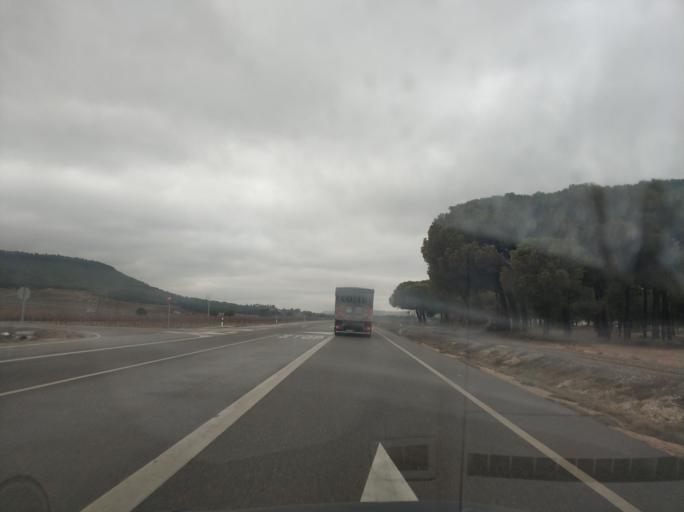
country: ES
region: Castille and Leon
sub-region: Provincia de Valladolid
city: Quintanilla de Onesimo
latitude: 41.6277
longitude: -4.3280
